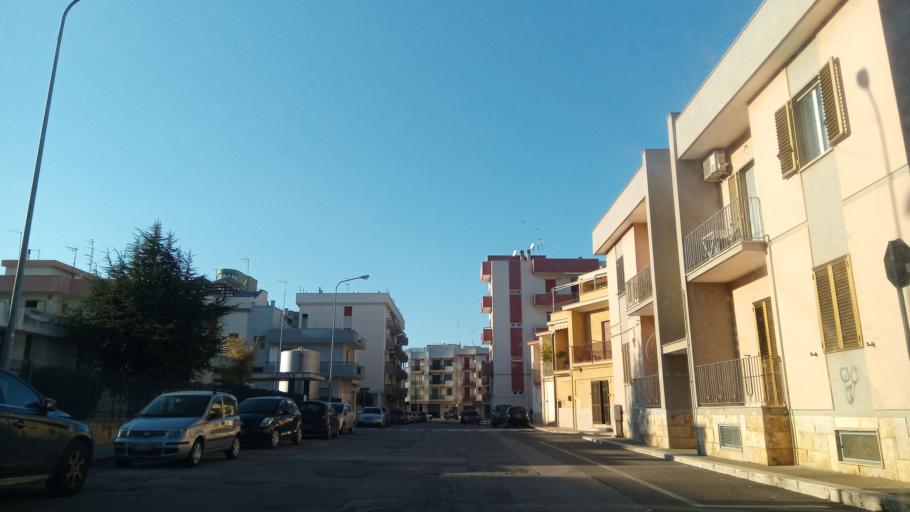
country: IT
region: Apulia
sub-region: Provincia di Bari
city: Polignano a Mare
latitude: 40.9902
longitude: 17.2250
